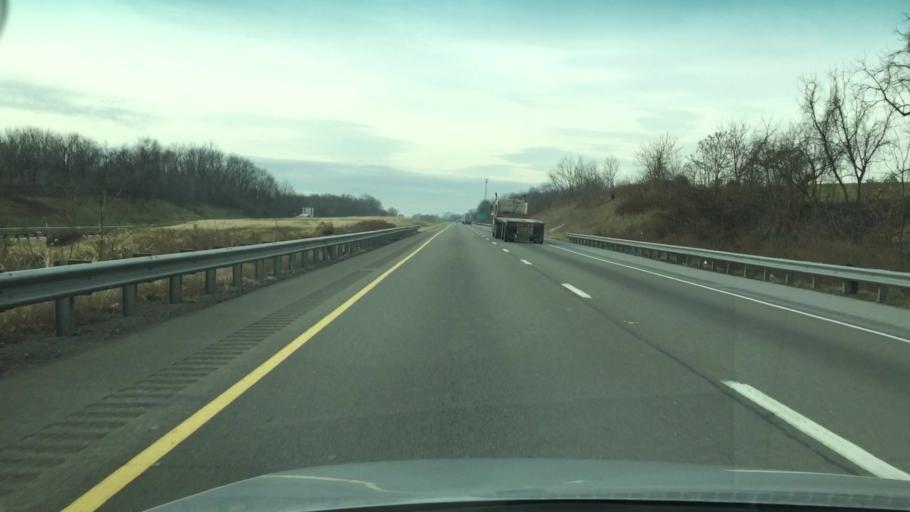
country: US
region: Pennsylvania
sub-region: Columbia County
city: Almedia
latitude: 41.0364
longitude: -76.3707
